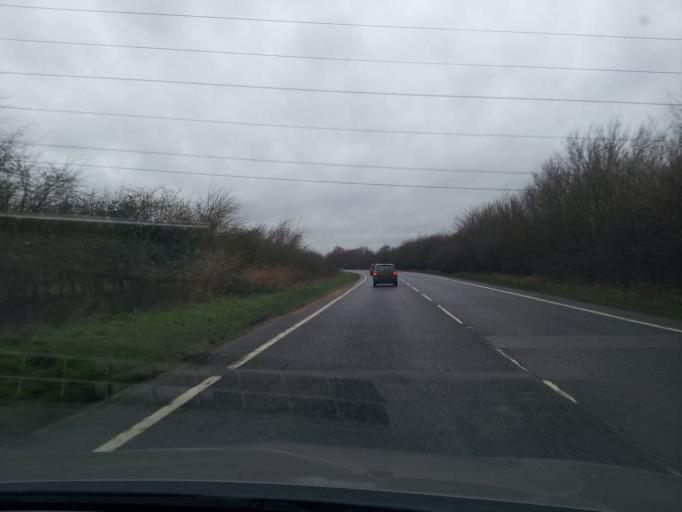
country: GB
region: England
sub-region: Norfolk
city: Diss
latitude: 52.3617
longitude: 1.1448
